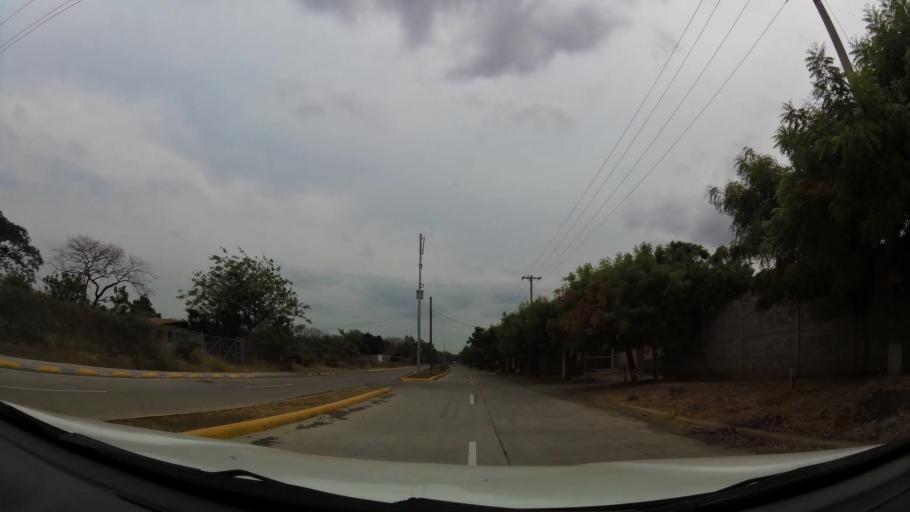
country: NI
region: Managua
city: Managua
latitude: 12.1168
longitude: -86.1713
